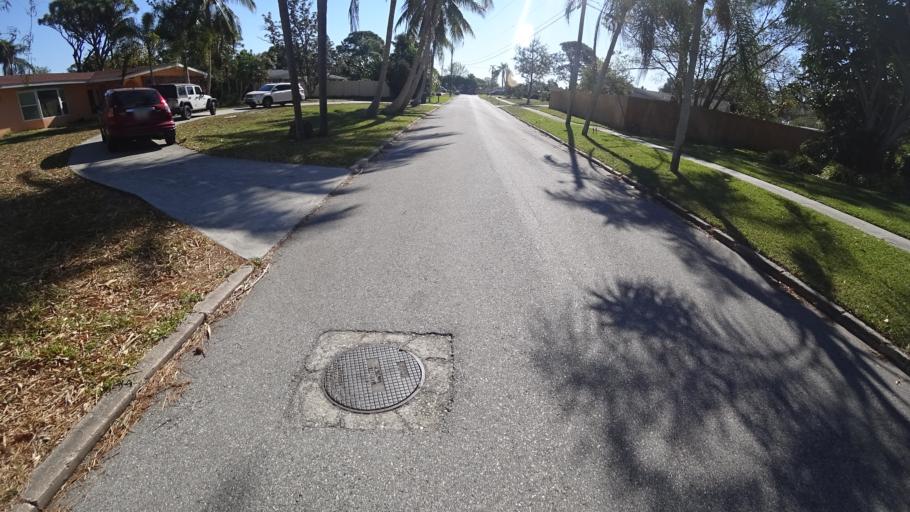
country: US
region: Florida
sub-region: Manatee County
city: West Bradenton
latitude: 27.4896
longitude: -82.6383
